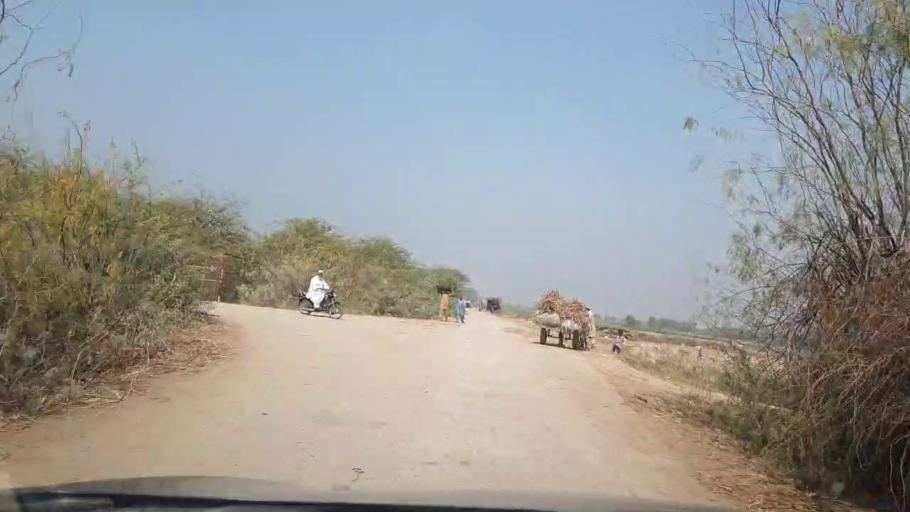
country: PK
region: Sindh
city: Tando Allahyar
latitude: 25.5002
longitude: 68.7960
